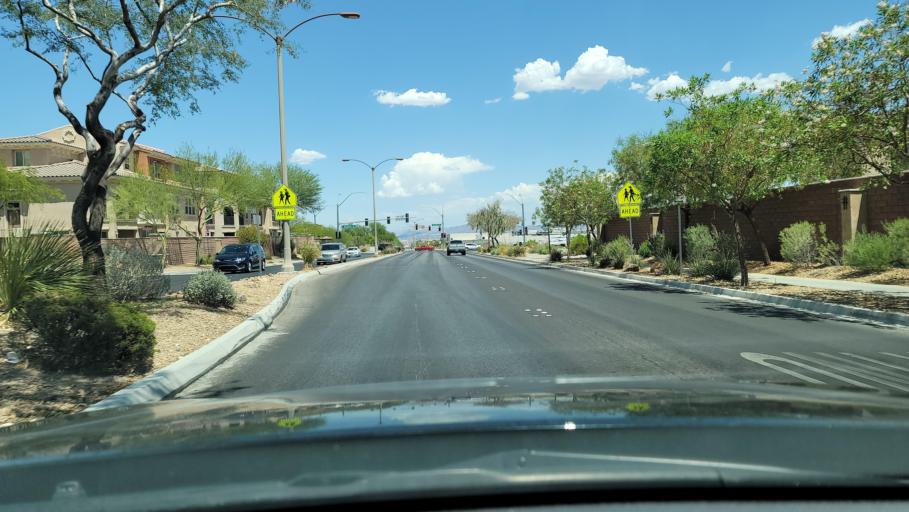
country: US
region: Nevada
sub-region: Clark County
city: Enterprise
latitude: 36.0053
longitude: -115.2634
